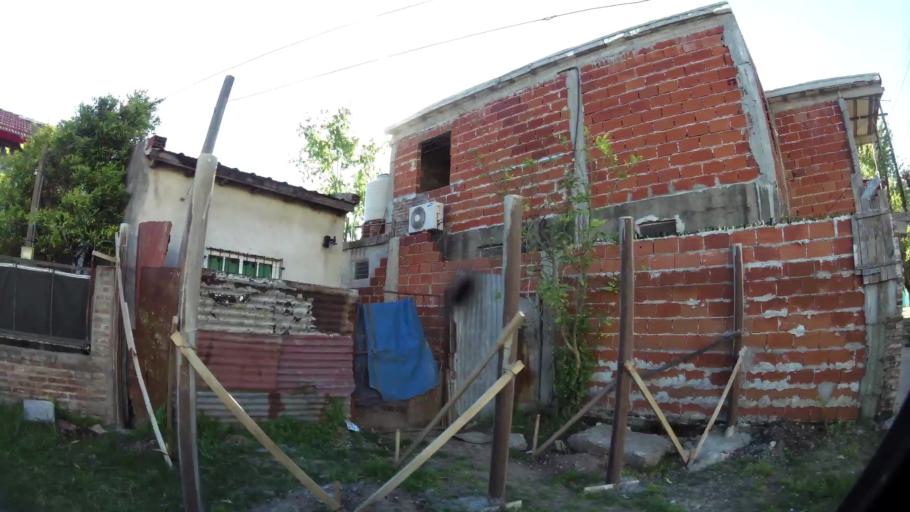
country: AR
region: Buenos Aires
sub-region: Partido de Quilmes
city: Quilmes
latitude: -34.7436
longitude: -58.3190
